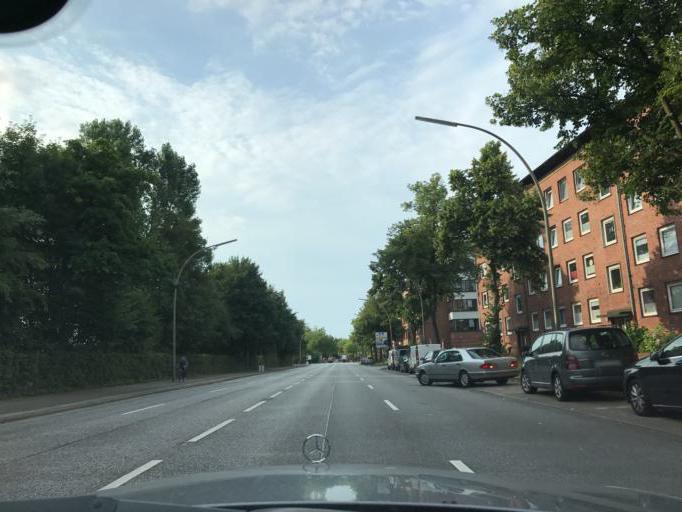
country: DE
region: Hamburg
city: Marienthal
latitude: 53.5580
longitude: 10.0818
